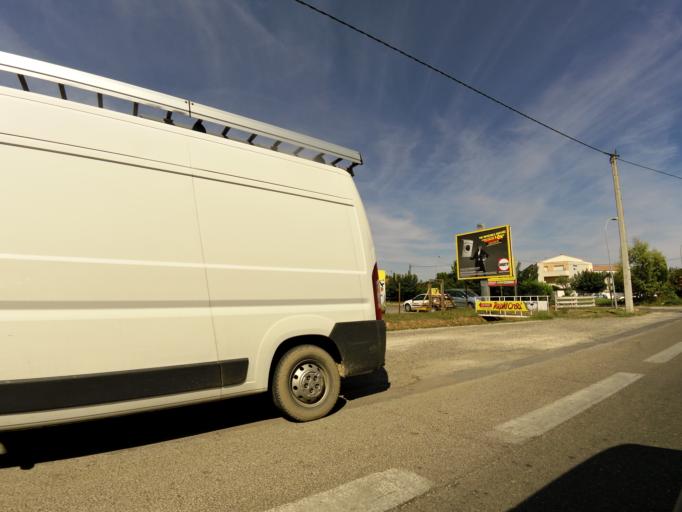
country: FR
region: Languedoc-Roussillon
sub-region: Departement de l'Herault
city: Lunel
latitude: 43.6772
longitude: 4.1212
